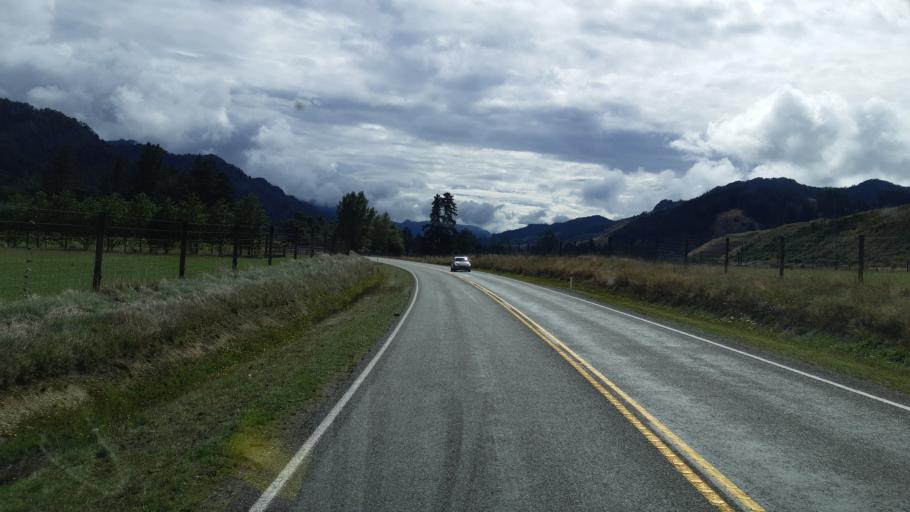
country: NZ
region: Tasman
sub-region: Tasman District
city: Wakefield
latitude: -41.7772
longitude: 172.3773
